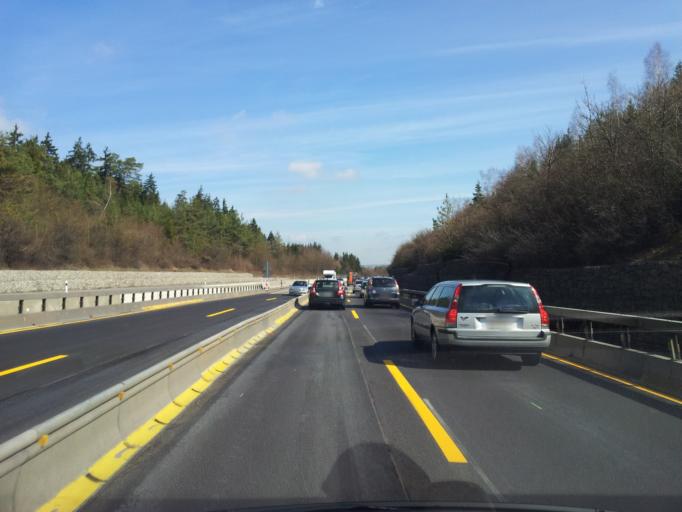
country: DE
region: Baden-Wuerttemberg
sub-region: Freiburg Region
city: Vohringen
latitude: 48.3077
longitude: 8.6374
